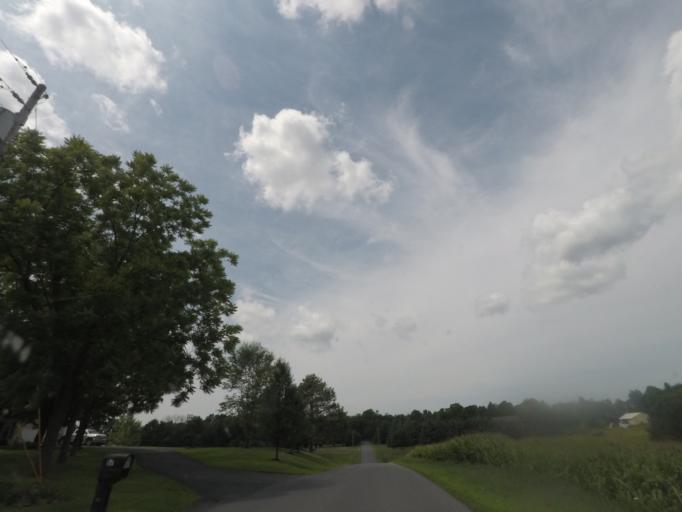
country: US
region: New York
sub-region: Rensselaer County
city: Wynantskill
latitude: 42.7129
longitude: -73.6132
